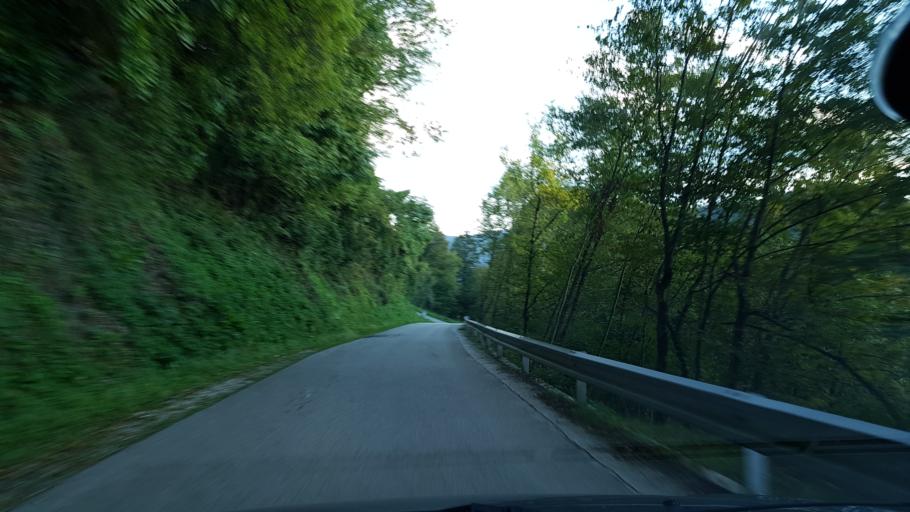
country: SI
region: Kobarid
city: Kobarid
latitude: 46.2649
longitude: 13.6084
